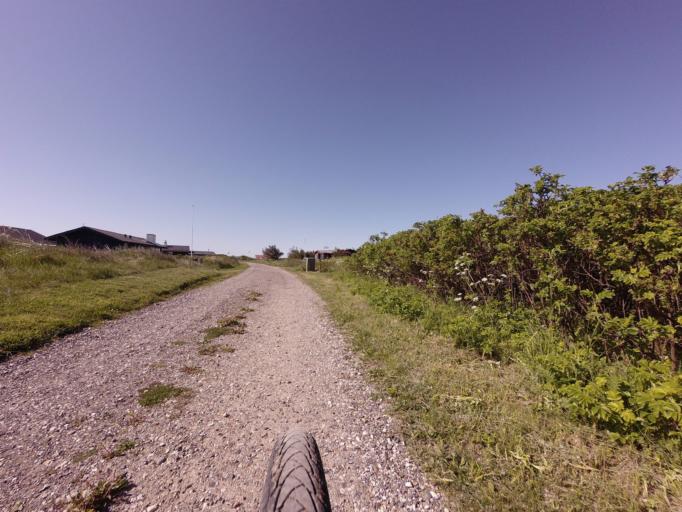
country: DK
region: North Denmark
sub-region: Jammerbugt Kommune
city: Pandrup
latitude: 57.3534
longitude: 9.6947
